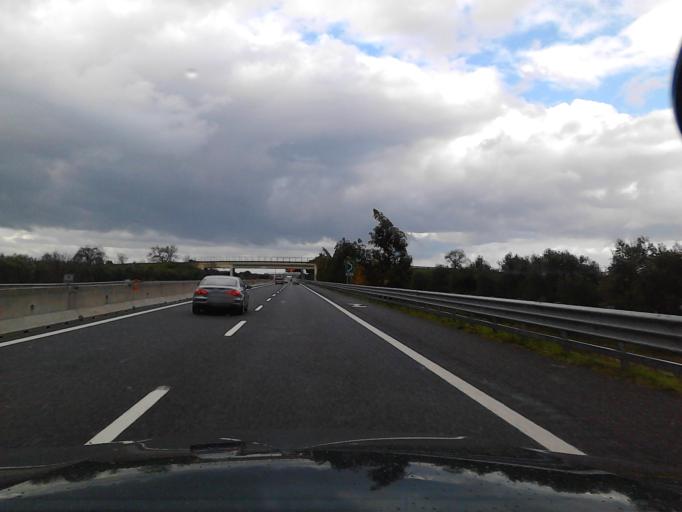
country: IT
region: Apulia
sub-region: Provincia di Bari
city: Molfetta
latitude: 41.1716
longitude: 16.5976
